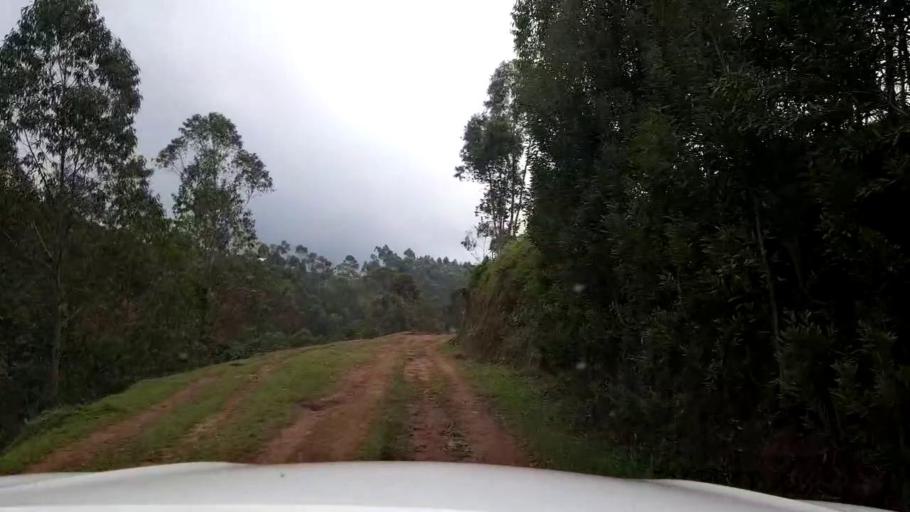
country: RW
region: Northern Province
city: Musanze
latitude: -1.5952
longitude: 29.7715
